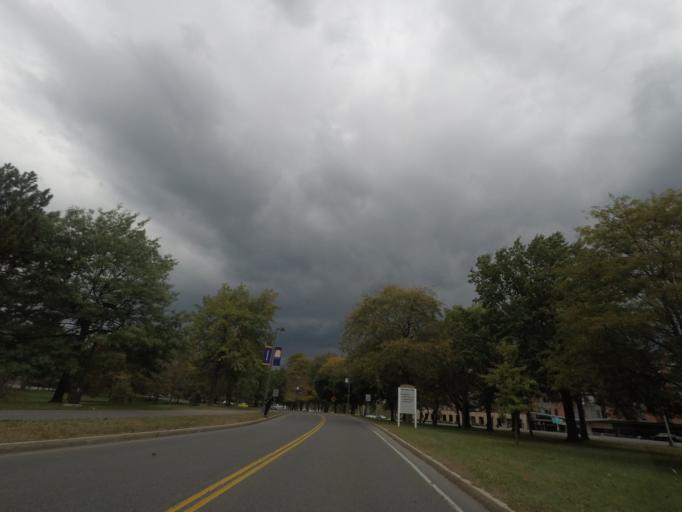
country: US
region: New York
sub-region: Albany County
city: Roessleville
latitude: 42.6899
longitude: -73.8222
